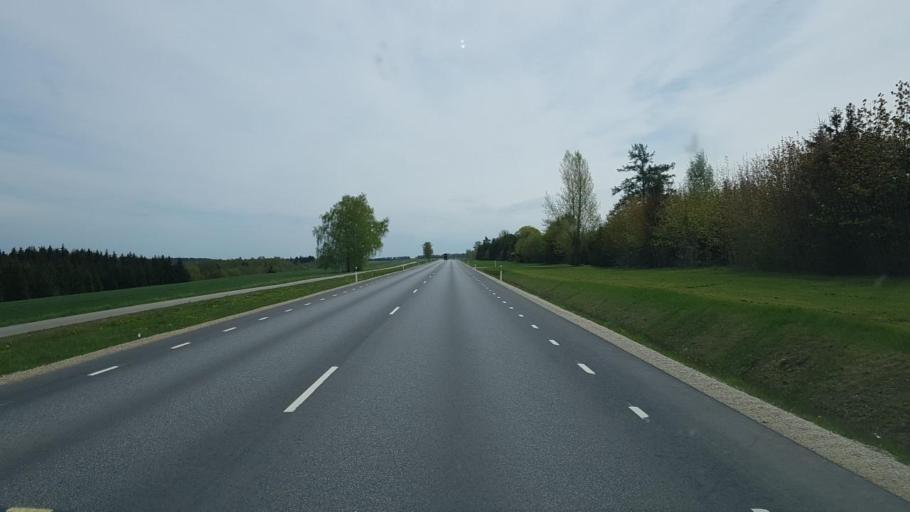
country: EE
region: Jogevamaa
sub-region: Tabivere vald
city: Tabivere
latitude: 58.6431
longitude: 26.5545
